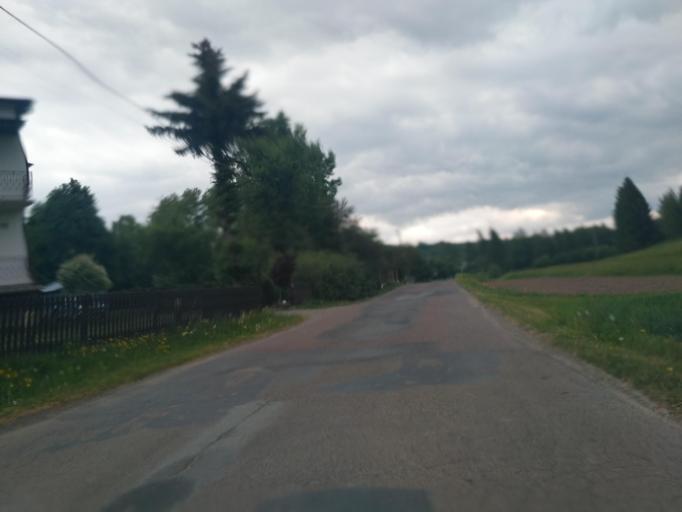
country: PL
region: Subcarpathian Voivodeship
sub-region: Powiat jasielski
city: Tarnowiec
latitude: 49.6727
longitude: 21.5766
